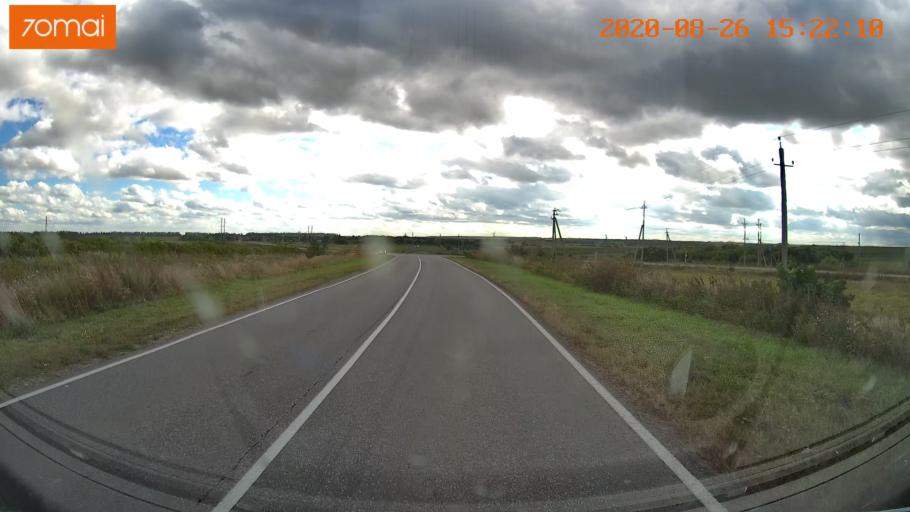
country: RU
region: Tula
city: Severo-Zadonsk
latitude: 54.1355
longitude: 38.4550
